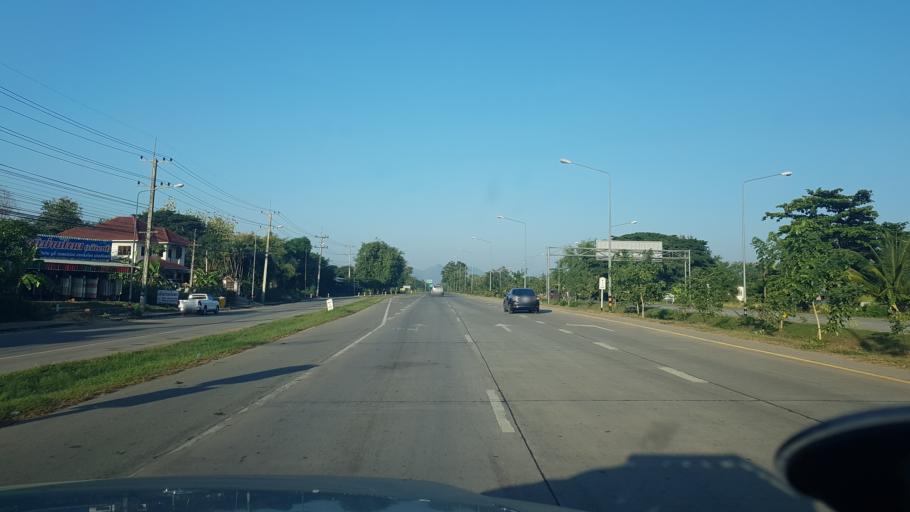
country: TH
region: Chaiyaphum
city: Khon San
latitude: 16.5894
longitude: 101.9969
